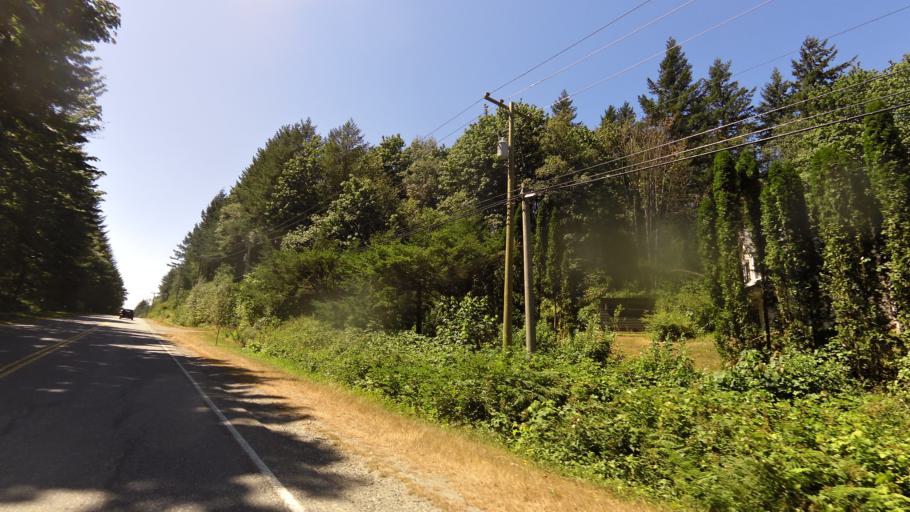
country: CA
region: British Columbia
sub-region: Fraser Valley Regional District
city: Chilliwack
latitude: 49.2027
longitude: -122.0368
